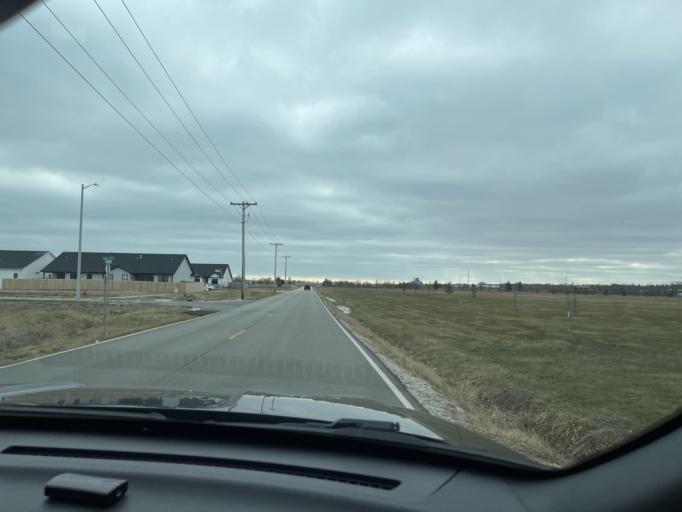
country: US
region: Illinois
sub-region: Sangamon County
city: Jerome
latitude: 39.7636
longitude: -89.7533
